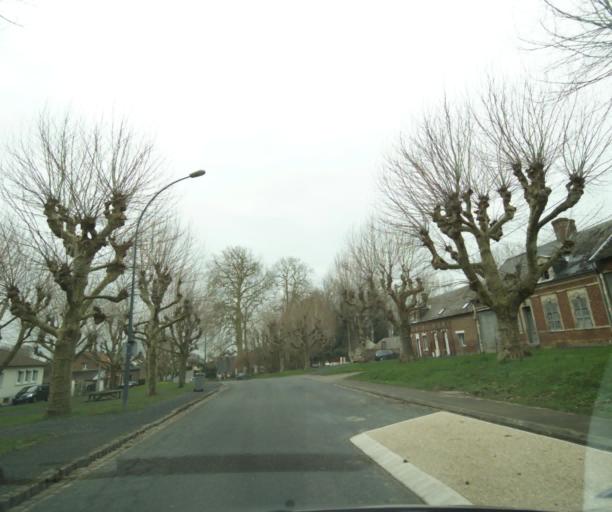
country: FR
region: Picardie
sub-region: Departement de l'Oise
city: Noyon
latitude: 49.5974
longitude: 3.0149
